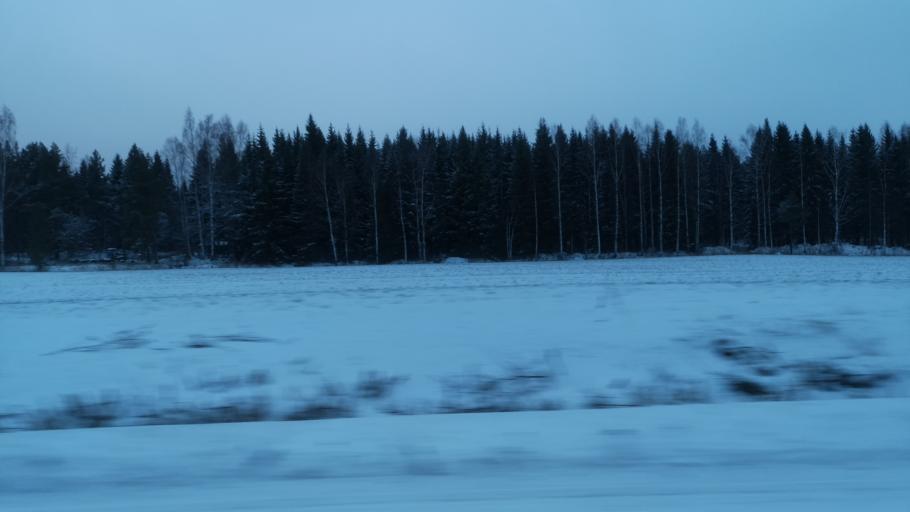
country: FI
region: Southern Savonia
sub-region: Savonlinna
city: Enonkoski
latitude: 62.0889
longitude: 28.6799
